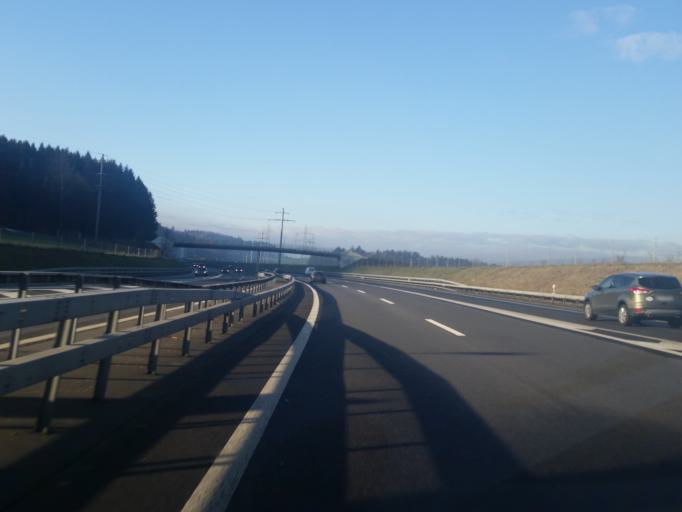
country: CH
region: Zurich
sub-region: Bezirk Affoltern
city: Obfelden / Toussen
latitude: 47.2734
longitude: 8.4371
